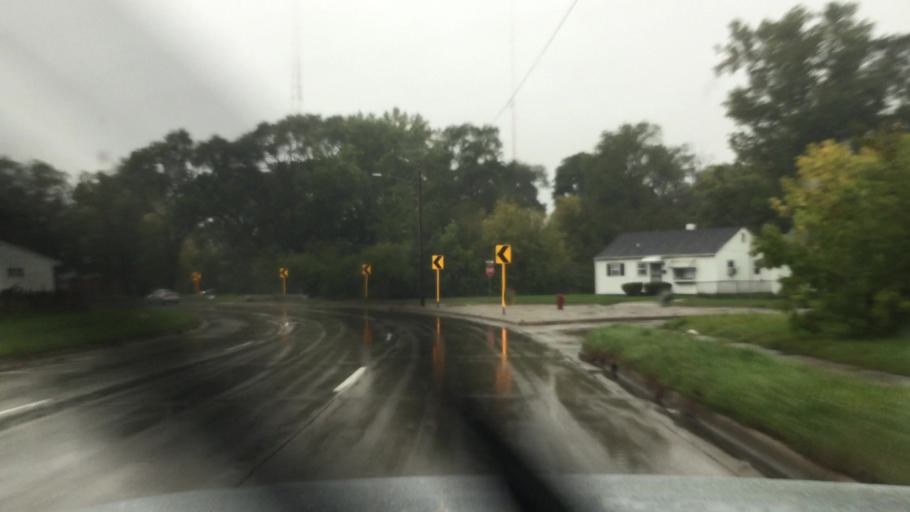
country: US
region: Michigan
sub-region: Saginaw County
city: Buena Vista
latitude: 43.4152
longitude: -83.9155
